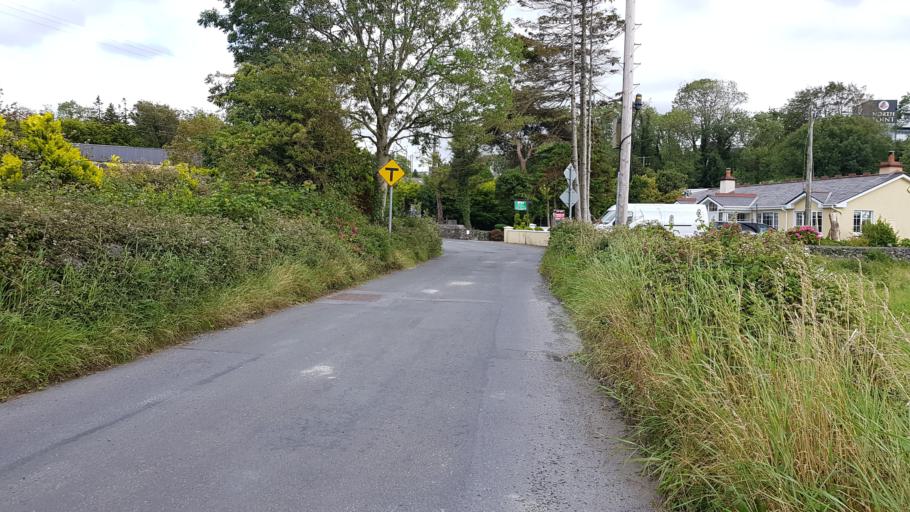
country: IE
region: Connaught
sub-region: County Galway
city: Gaillimh
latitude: 53.2961
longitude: -9.0183
